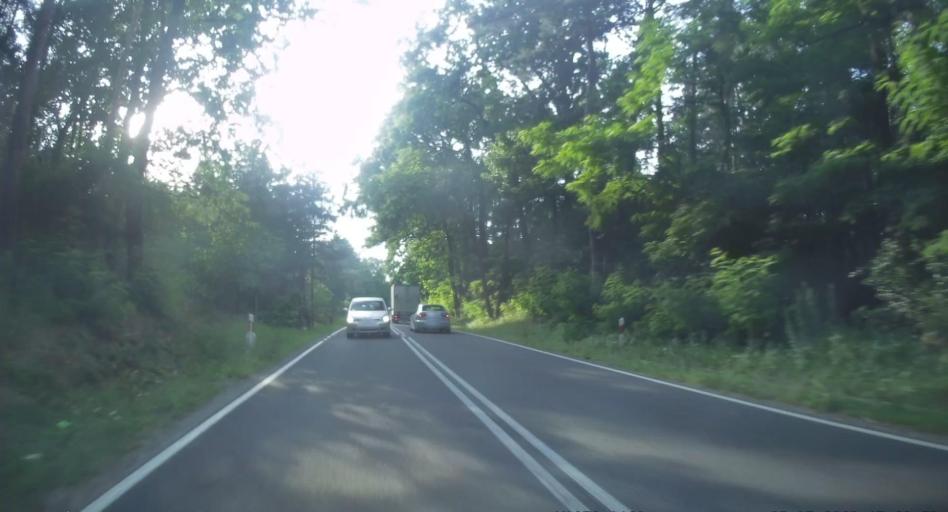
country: PL
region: Lesser Poland Voivodeship
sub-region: Powiat brzeski
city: Przyborow
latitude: 50.0457
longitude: 20.6450
